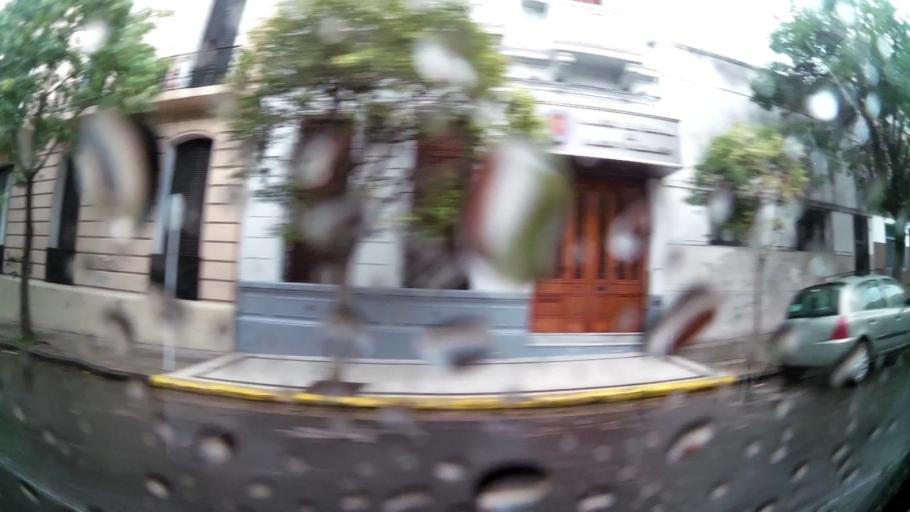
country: AR
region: Buenos Aires F.D.
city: Buenos Aires
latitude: -34.6283
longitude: -58.3749
